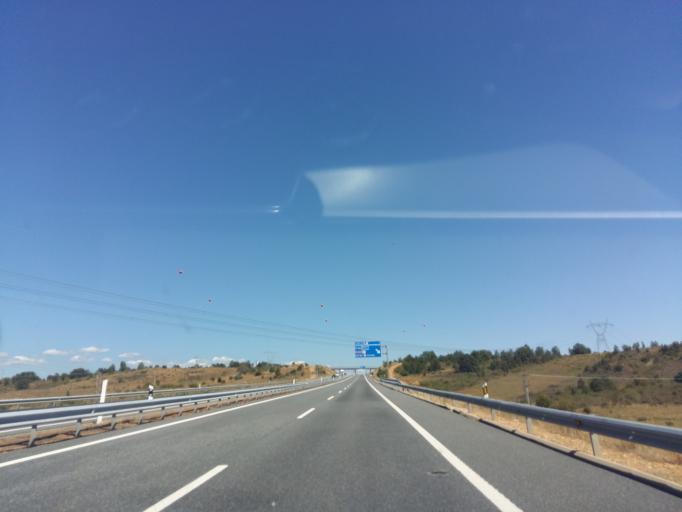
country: ES
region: Castille and Leon
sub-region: Provincia de Leon
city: Valverde de la Virgen
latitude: 42.5618
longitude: -5.6737
